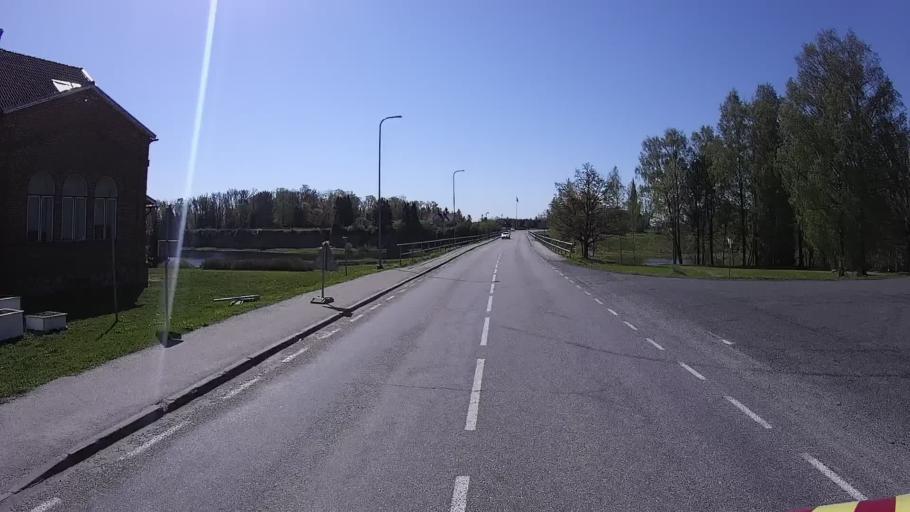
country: EE
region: Paernumaa
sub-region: Tootsi vald
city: Tootsi
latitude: 58.4857
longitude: 24.8140
